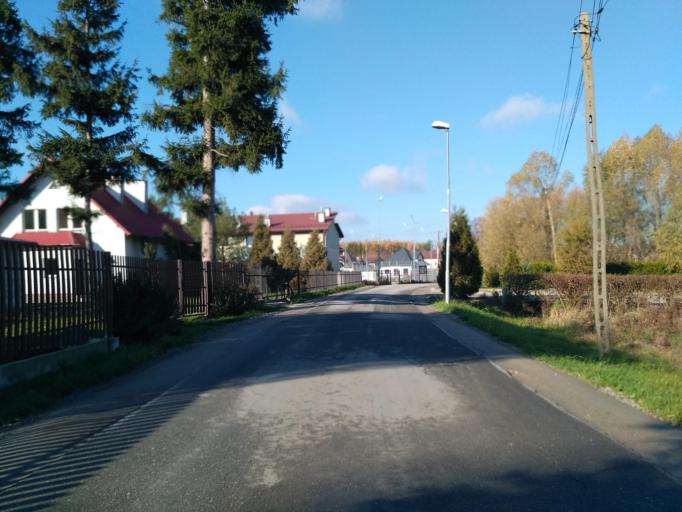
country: PL
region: Subcarpathian Voivodeship
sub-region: Powiat rzeszowski
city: Niechobrz
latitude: 50.0098
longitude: 21.8960
